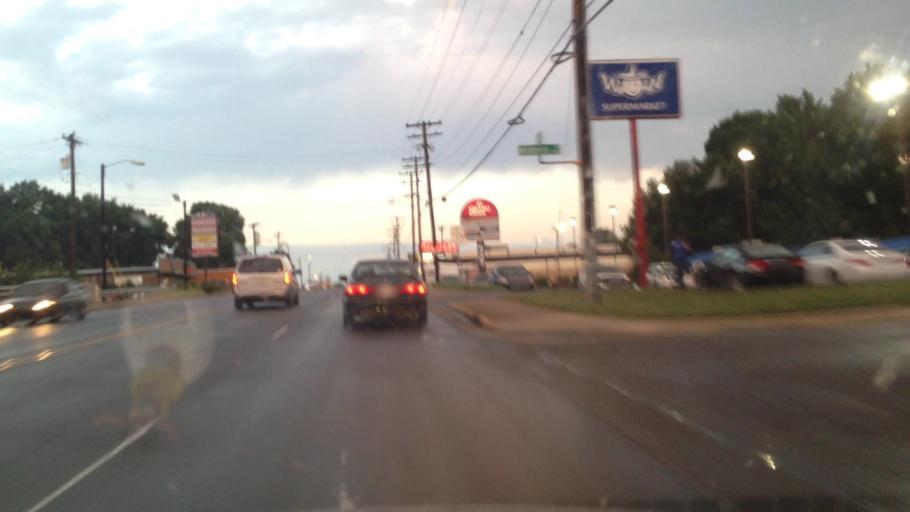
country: US
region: North Carolina
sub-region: Mecklenburg County
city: Pineville
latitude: 35.1467
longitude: -80.8764
